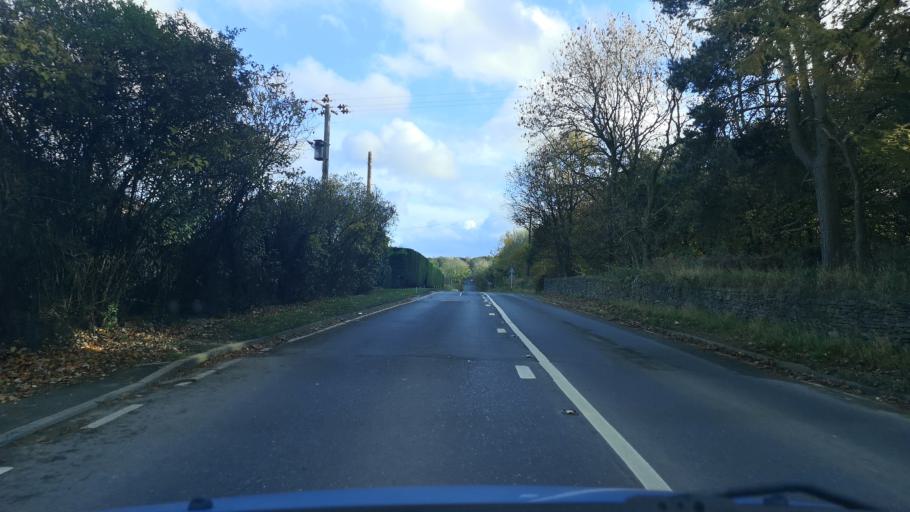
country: GB
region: England
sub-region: Kirklees
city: Mirfield
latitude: 53.6496
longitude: -1.6846
